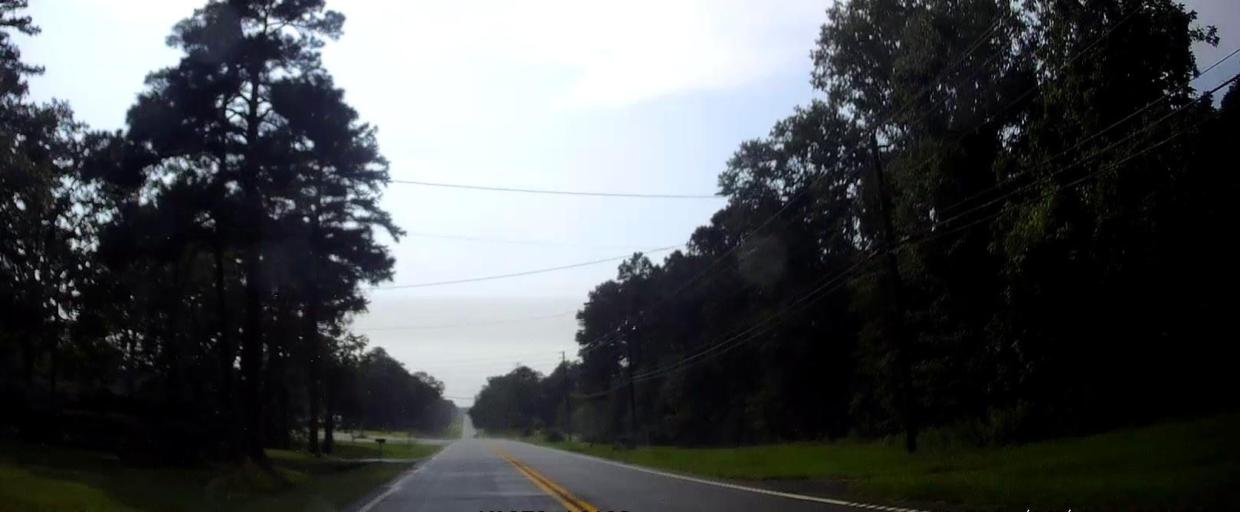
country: US
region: Georgia
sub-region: Twiggs County
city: Jeffersonville
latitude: 32.6044
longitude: -83.2521
